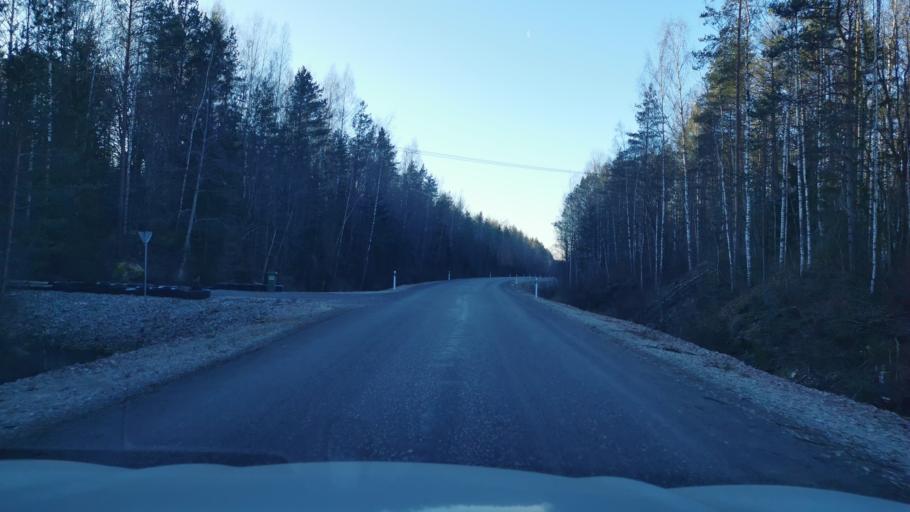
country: EE
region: Ida-Virumaa
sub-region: Kohtla-Nomme vald
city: Kohtla-Nomme
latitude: 59.3432
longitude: 27.1471
